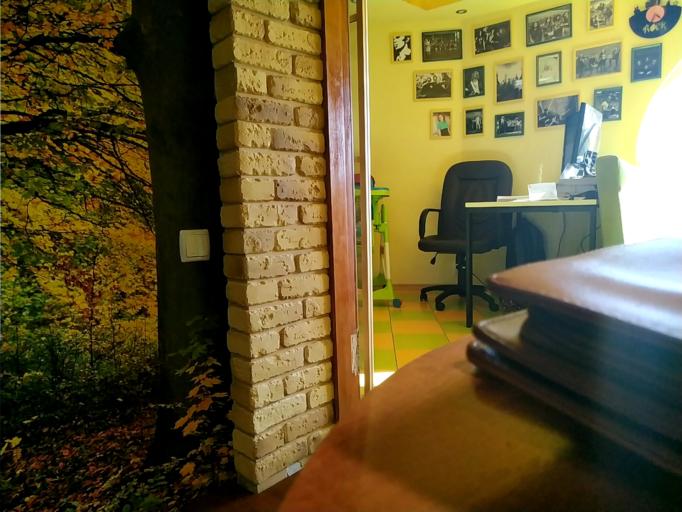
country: RU
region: Vologda
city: Nelazskoye
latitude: 59.4259
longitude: 37.6079
